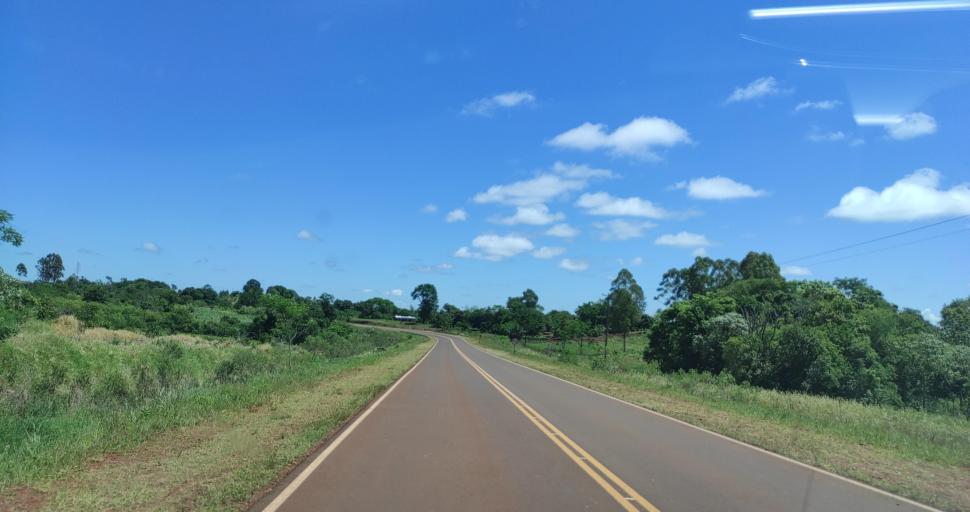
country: AR
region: Misiones
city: Campo Grande
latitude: -27.3274
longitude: -54.8911
